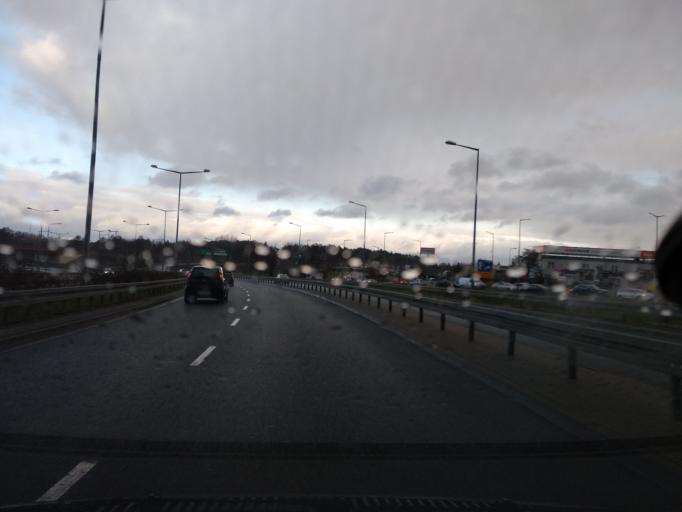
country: PL
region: Greater Poland Voivodeship
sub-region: Powiat koninski
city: Stare Miasto
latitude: 52.1857
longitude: 18.2286
